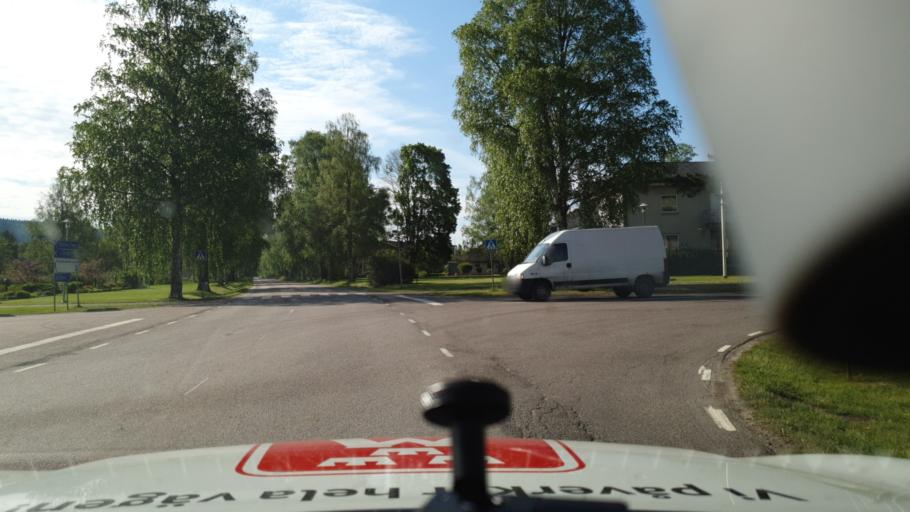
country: SE
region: Vaermland
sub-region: Torsby Kommun
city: Torsby
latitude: 59.9462
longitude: 12.9113
